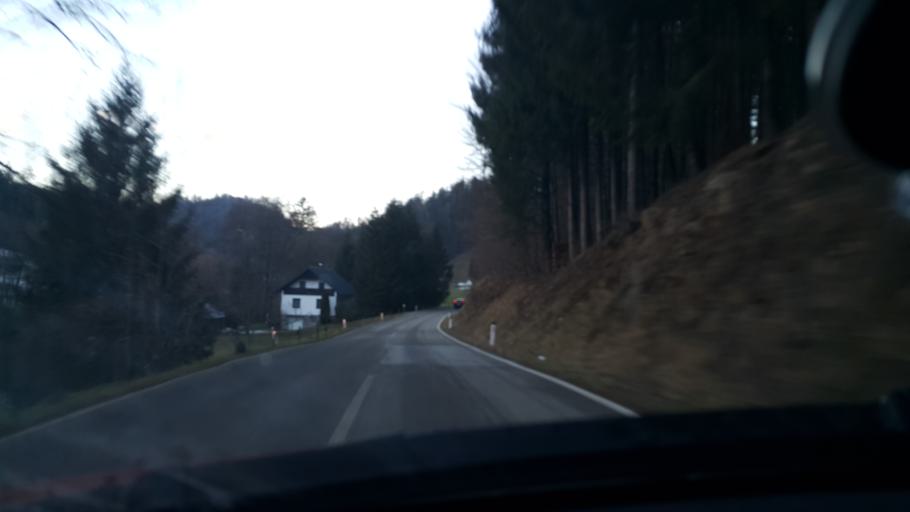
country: AT
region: Styria
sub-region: Politischer Bezirk Graz-Umgebung
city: Stiwoll
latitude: 47.1076
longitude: 15.2153
